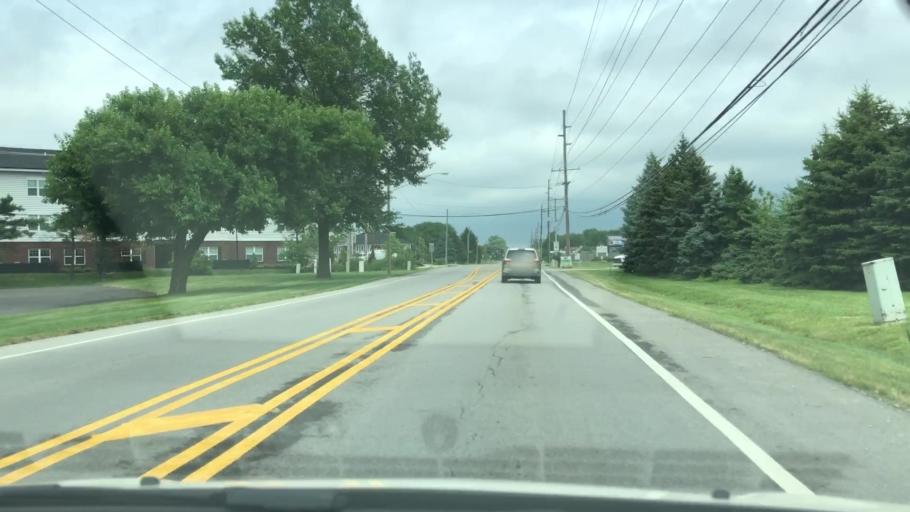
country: US
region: Ohio
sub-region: Franklin County
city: Worthington
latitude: 40.1153
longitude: -82.9913
